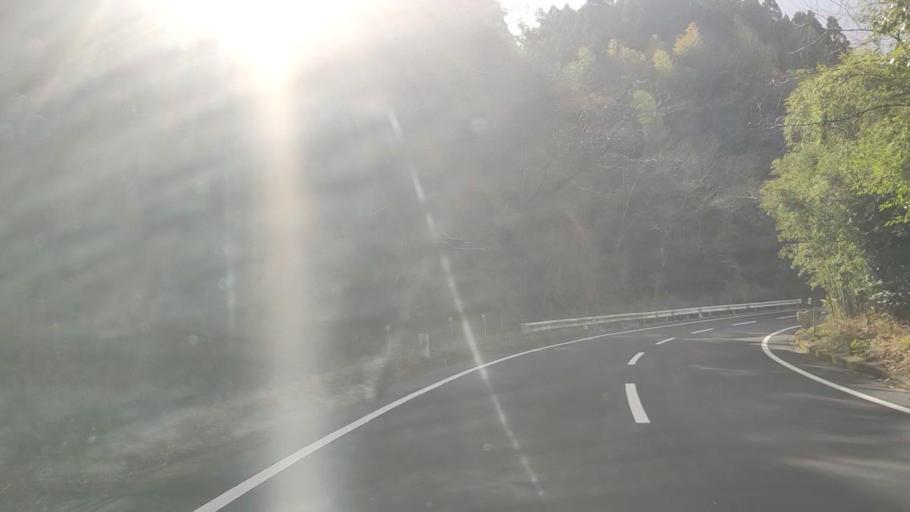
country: JP
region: Kagoshima
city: Okuchi-shinohara
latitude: 31.9587
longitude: 130.7345
